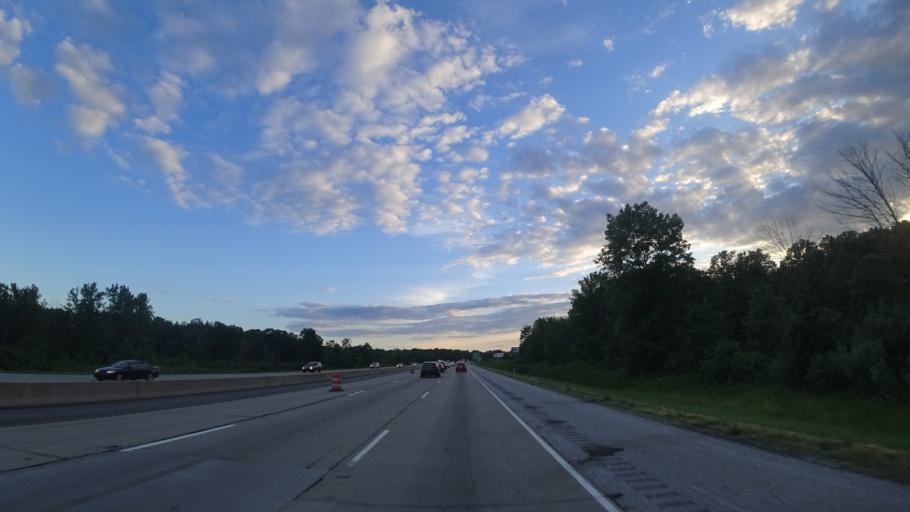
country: US
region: Indiana
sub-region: Porter County
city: Chesterton
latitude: 41.6300
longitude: -87.0176
